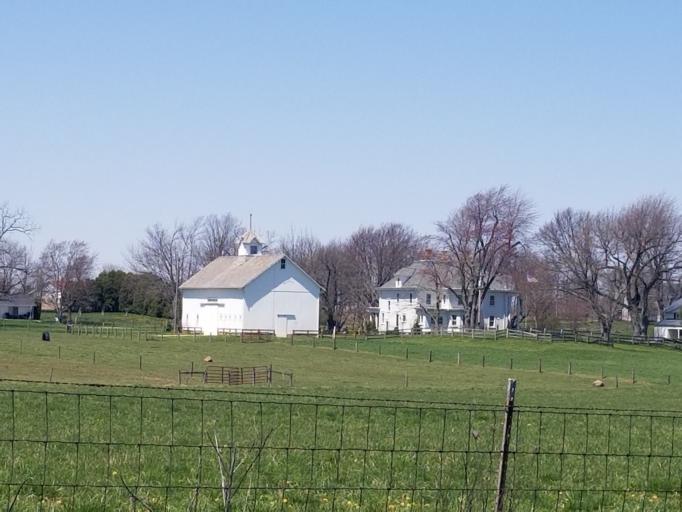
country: US
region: Ohio
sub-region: Huron County
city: New London
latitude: 41.0858
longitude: -82.4378
